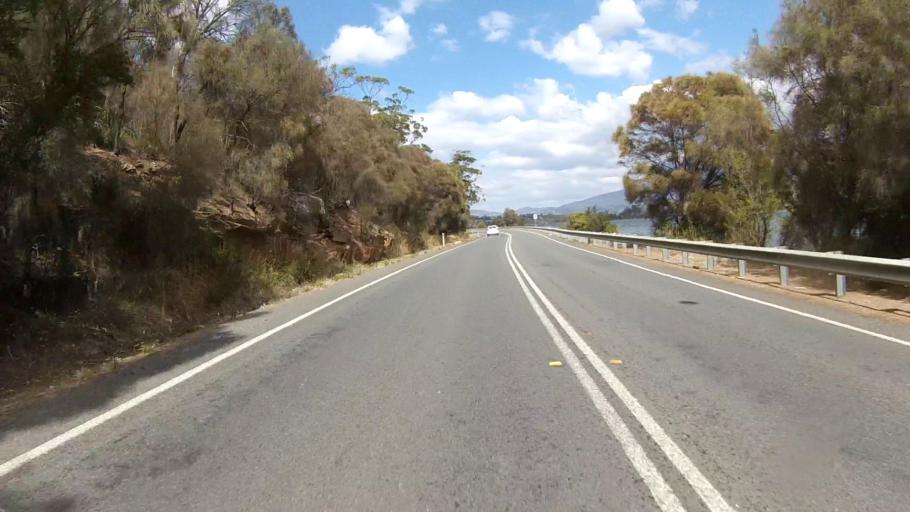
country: AU
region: Tasmania
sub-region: Brighton
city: Old Beach
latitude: -42.7797
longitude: 147.2853
